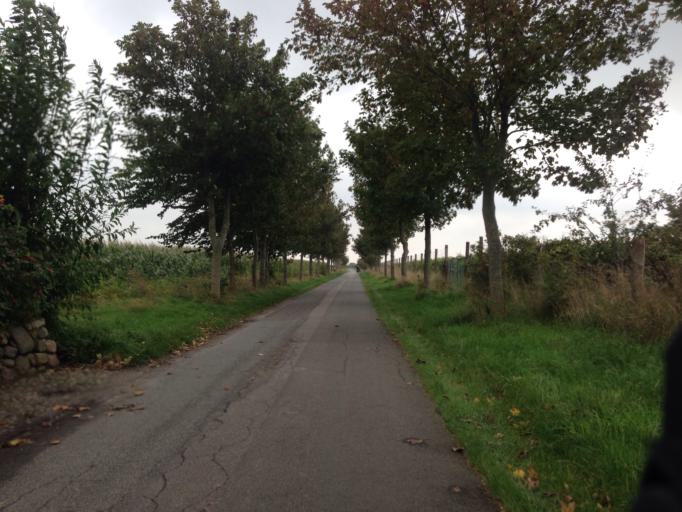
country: DE
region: Schleswig-Holstein
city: Alkersum
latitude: 54.7049
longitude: 8.5047
